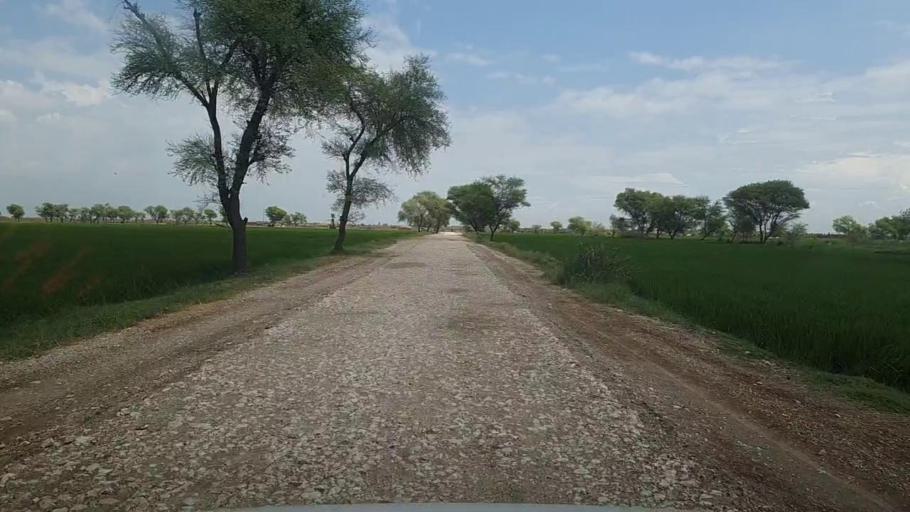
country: PK
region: Sindh
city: Kandhkot
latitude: 28.3421
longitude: 69.2187
